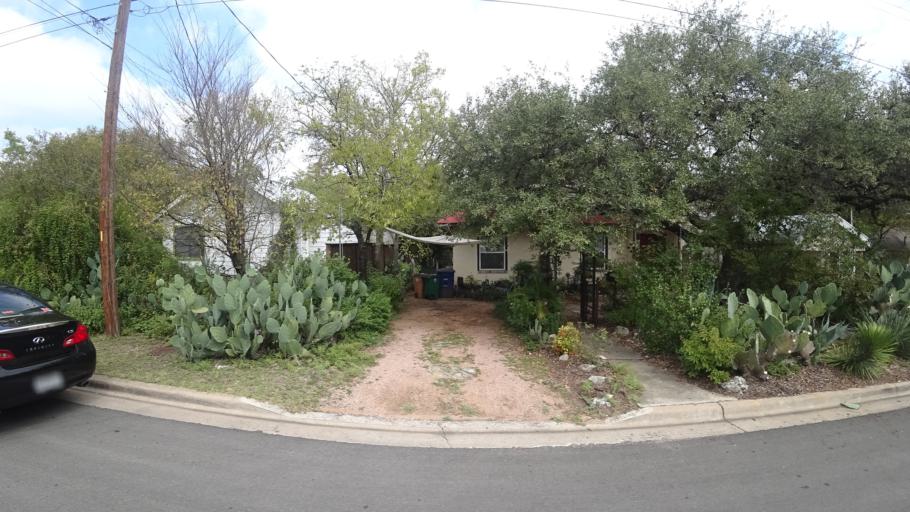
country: US
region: Texas
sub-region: Travis County
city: Austin
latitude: 30.2514
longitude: -97.7563
